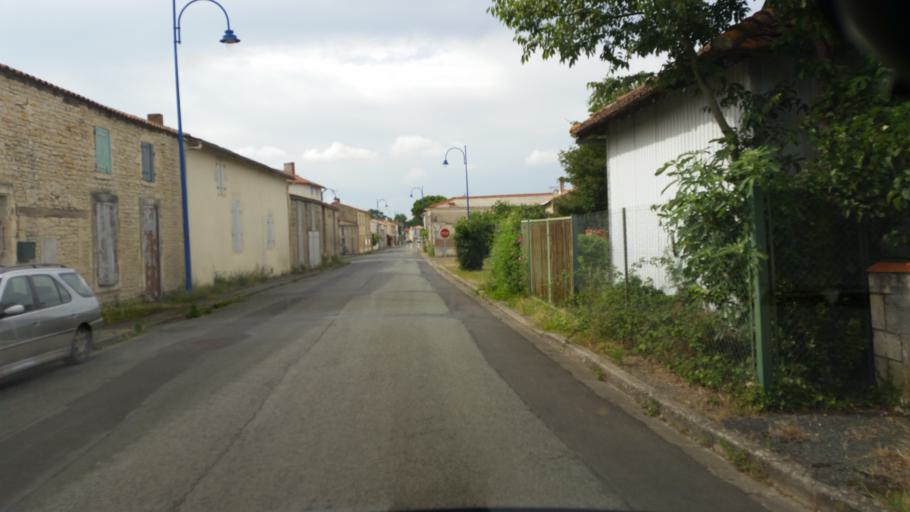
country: FR
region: Poitou-Charentes
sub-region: Departement de la Charente-Maritime
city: Courcon
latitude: 46.1851
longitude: -0.8599
